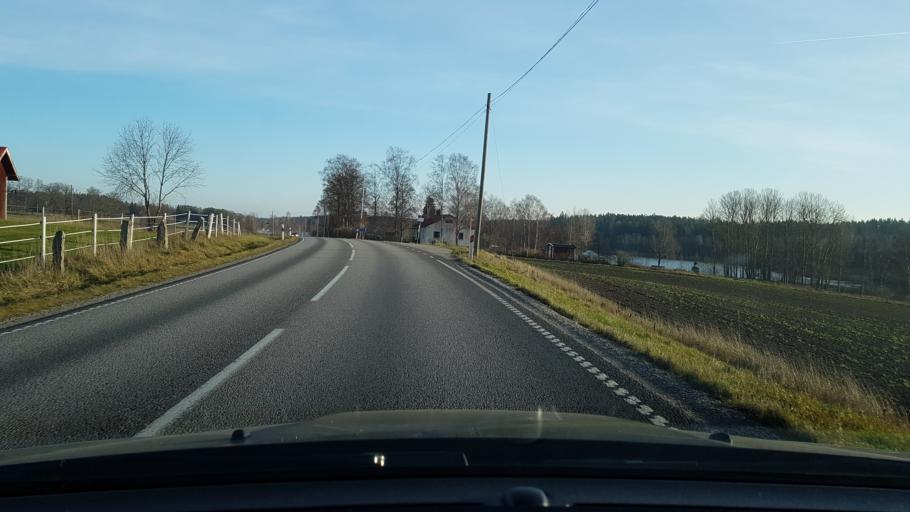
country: SE
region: Stockholm
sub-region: Norrtalje Kommun
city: Nykvarn
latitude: 59.7354
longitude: 18.2503
